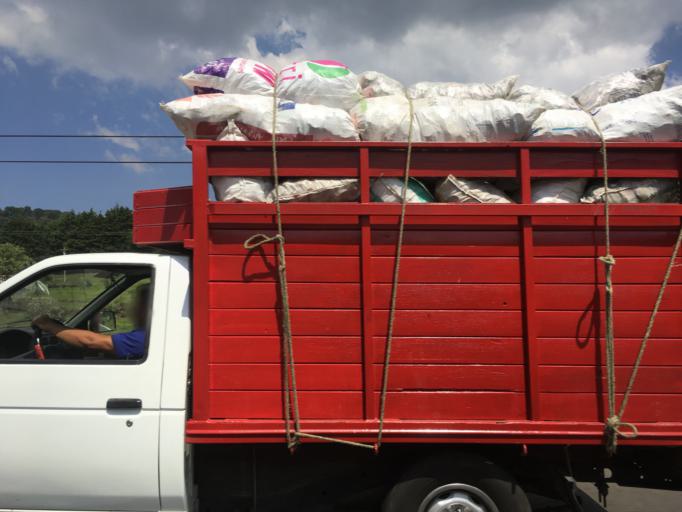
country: MX
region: Mexico
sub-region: Morelos
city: San Marcos Tlazalpan
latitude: 19.8329
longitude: -99.7046
